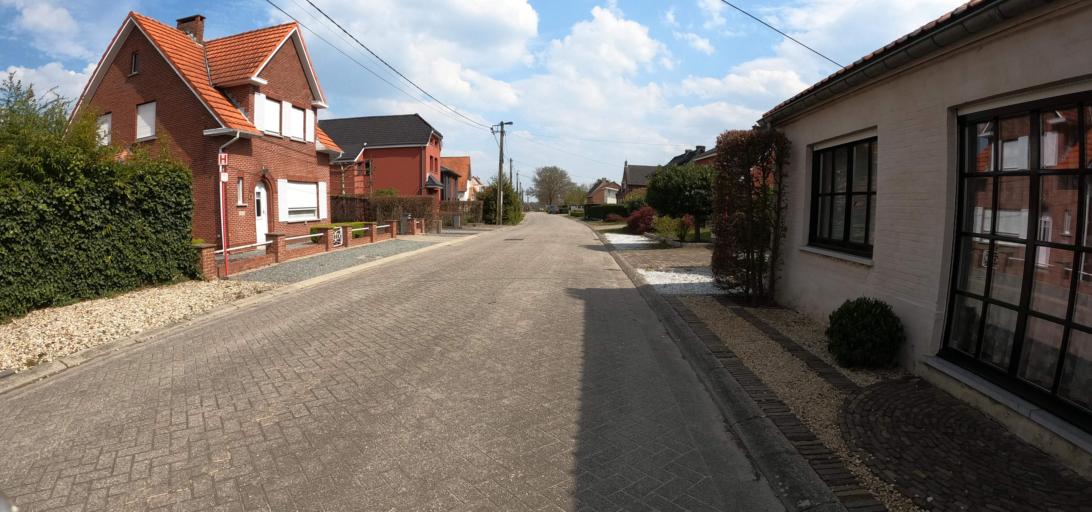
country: BE
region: Flanders
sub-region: Provincie Antwerpen
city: Oostmalle
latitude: 51.3004
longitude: 4.7479
